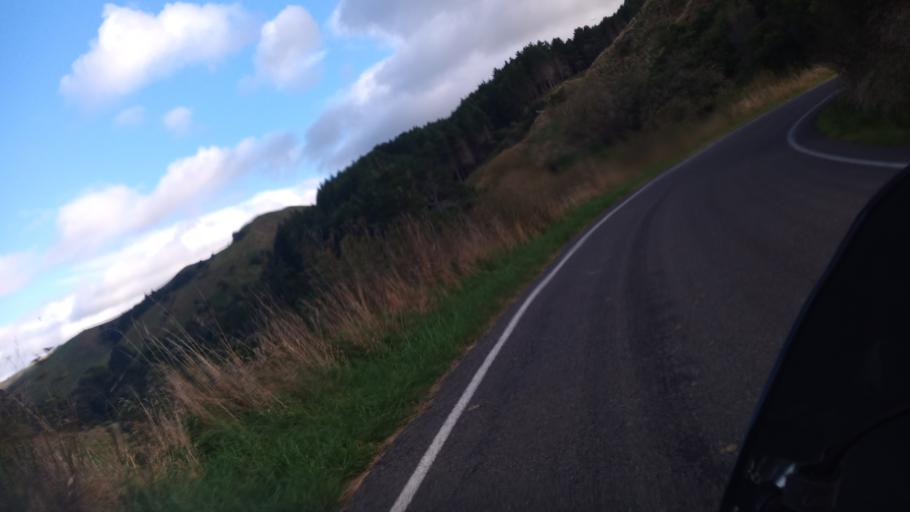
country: NZ
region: Gisborne
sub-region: Gisborne District
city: Gisborne
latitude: -38.5318
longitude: 177.5497
